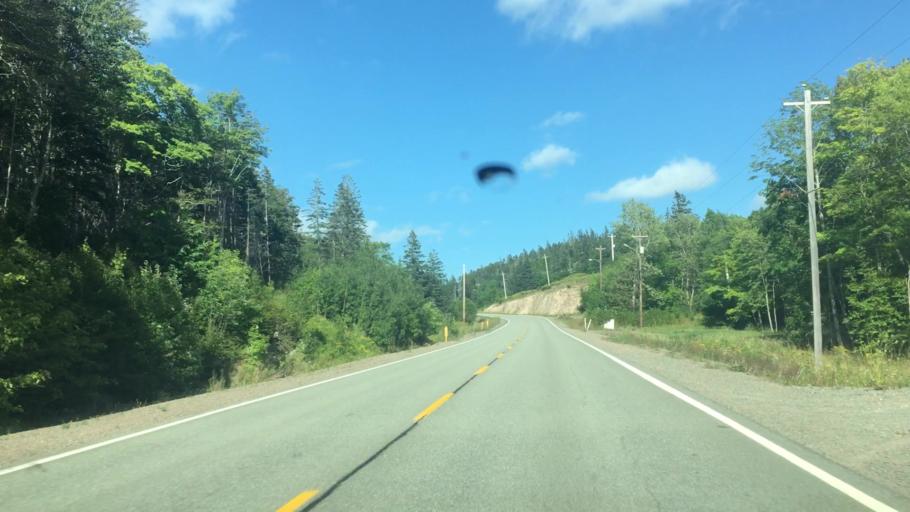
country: CA
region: Nova Scotia
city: Sydney
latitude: 45.8511
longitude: -60.6364
